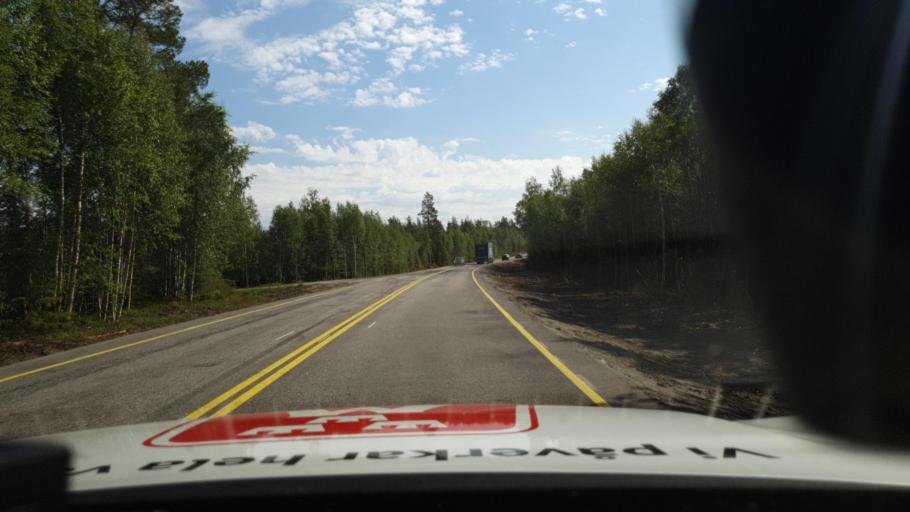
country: SE
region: Norrbotten
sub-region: Lulea Kommun
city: Ranea
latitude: 65.8716
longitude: 22.3434
